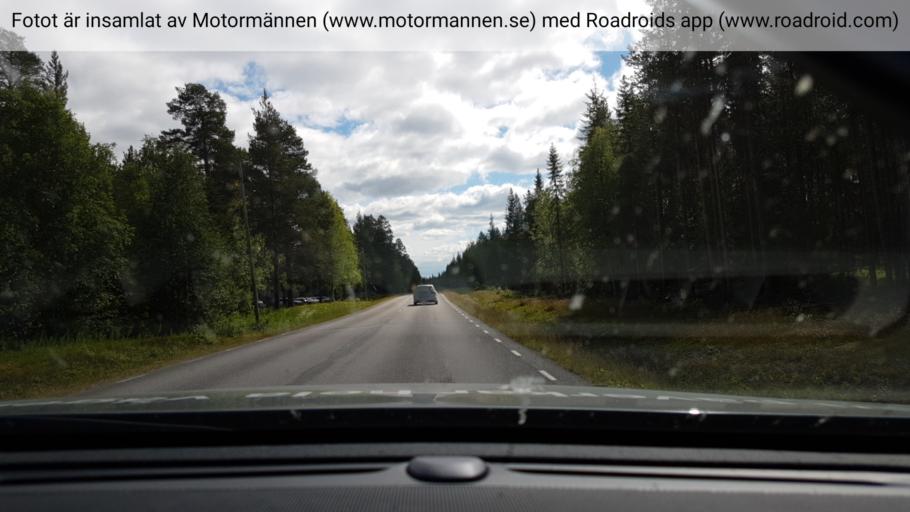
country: SE
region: Vaesterbotten
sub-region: Sorsele Kommun
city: Sorsele
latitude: 65.5669
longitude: 17.5237
